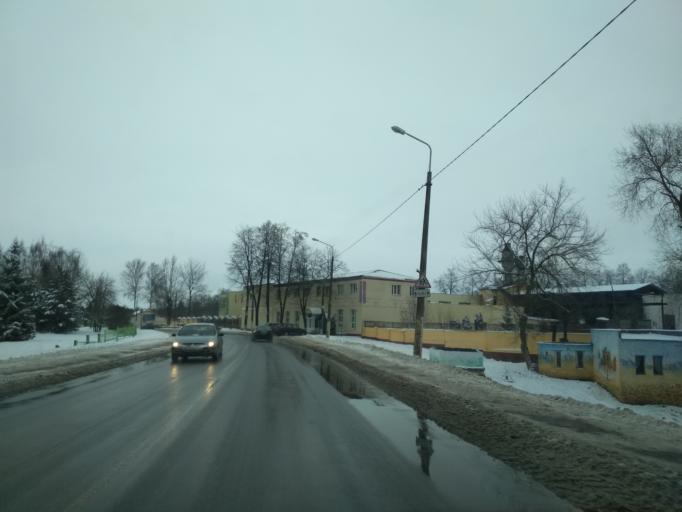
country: BY
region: Minsk
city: Mar''ina Horka
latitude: 53.5228
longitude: 28.1403
